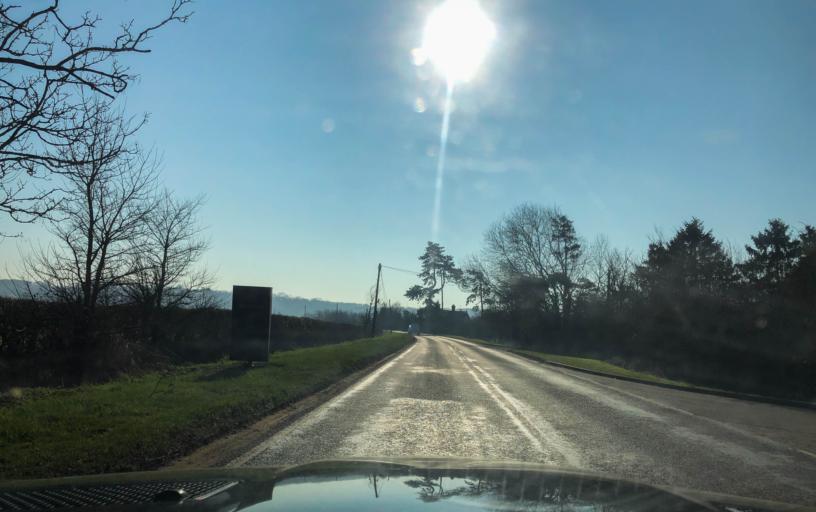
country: GB
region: England
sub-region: Warwickshire
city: Wellesbourne Mountford
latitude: 52.1892
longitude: -1.5834
